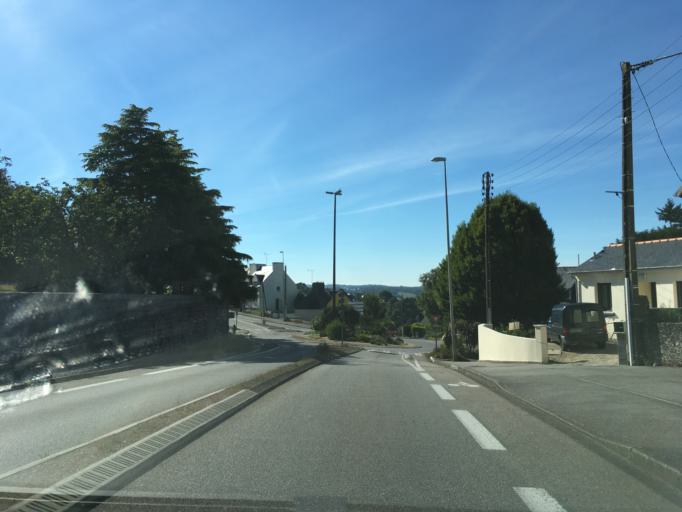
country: FR
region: Brittany
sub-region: Departement du Finistere
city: Quimper
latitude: 47.9882
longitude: -4.0867
